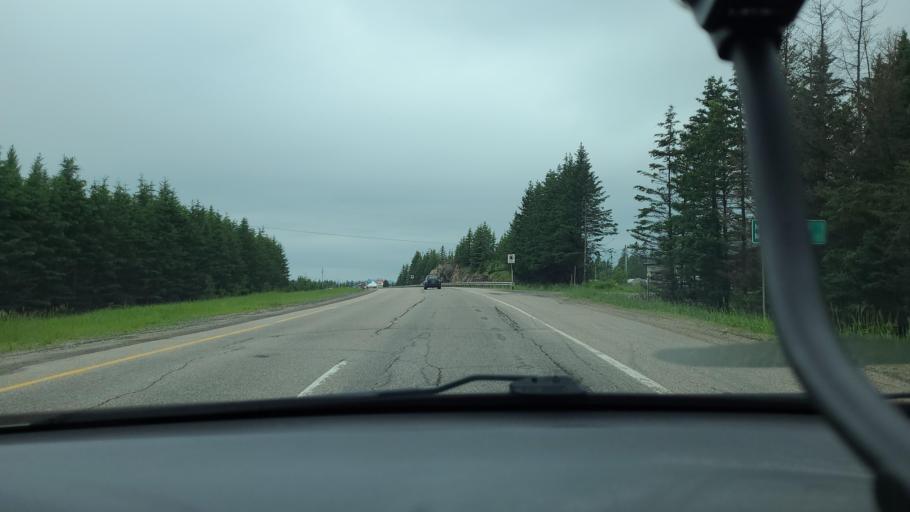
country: CA
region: Quebec
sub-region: Laurentides
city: Mont-Tremblant
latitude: 46.1107
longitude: -74.4949
